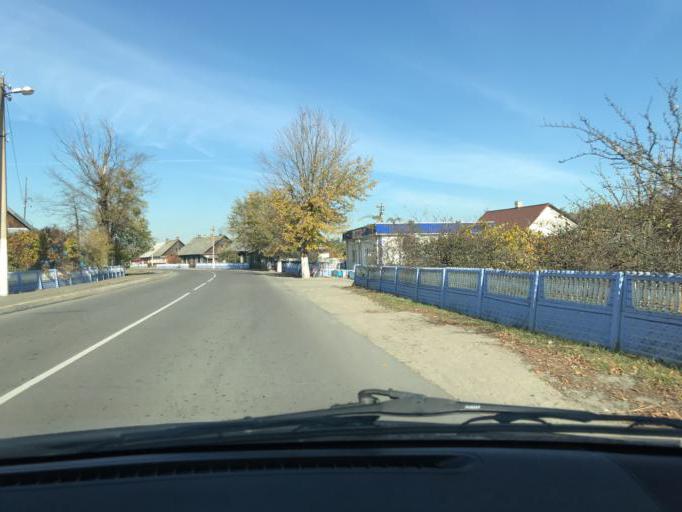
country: BY
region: Brest
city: Mikashevichy
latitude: 52.2269
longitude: 27.4599
